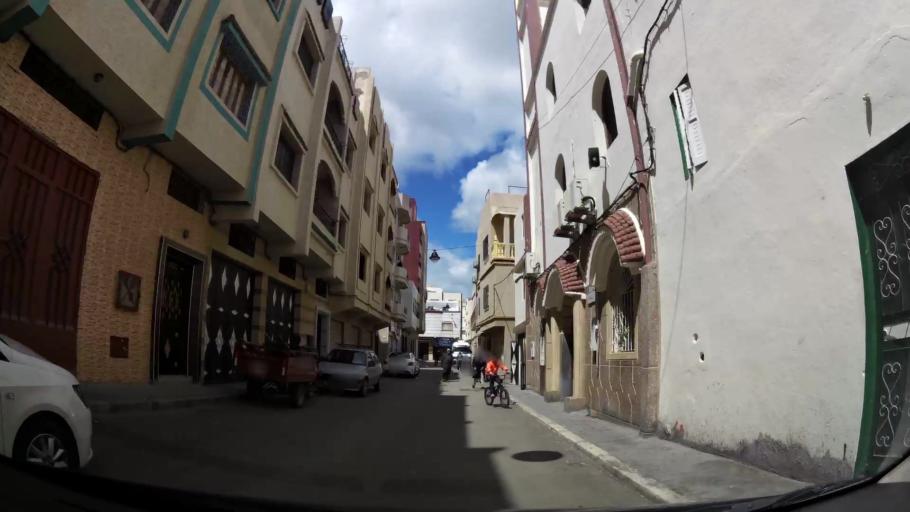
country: MA
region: Tanger-Tetouan
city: Tetouan
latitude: 35.5798
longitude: -5.3497
